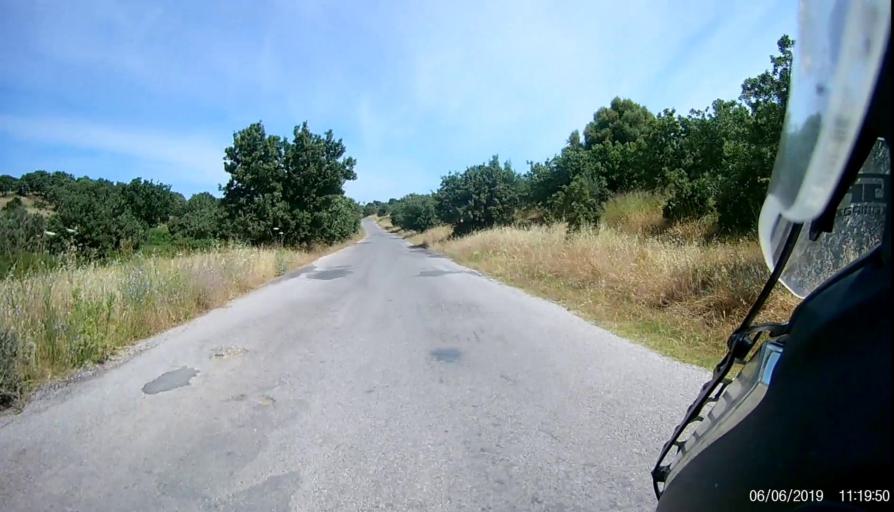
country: TR
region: Canakkale
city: Gulpinar
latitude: 39.6606
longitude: 26.1641
